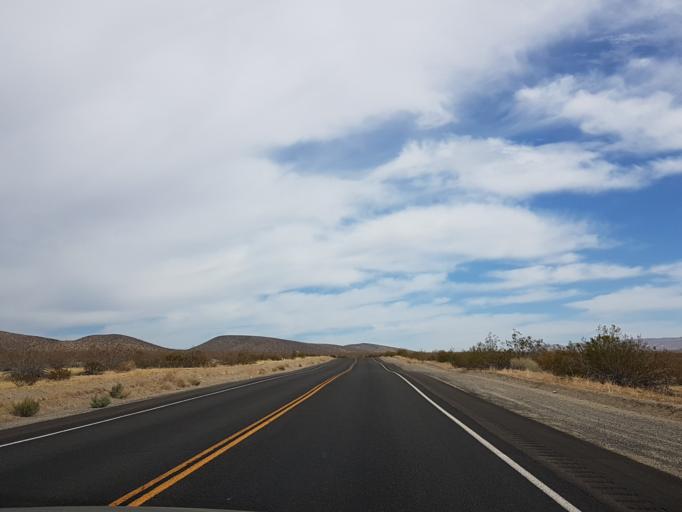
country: US
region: California
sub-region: Kern County
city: Ridgecrest
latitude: 35.4268
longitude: -117.6842
